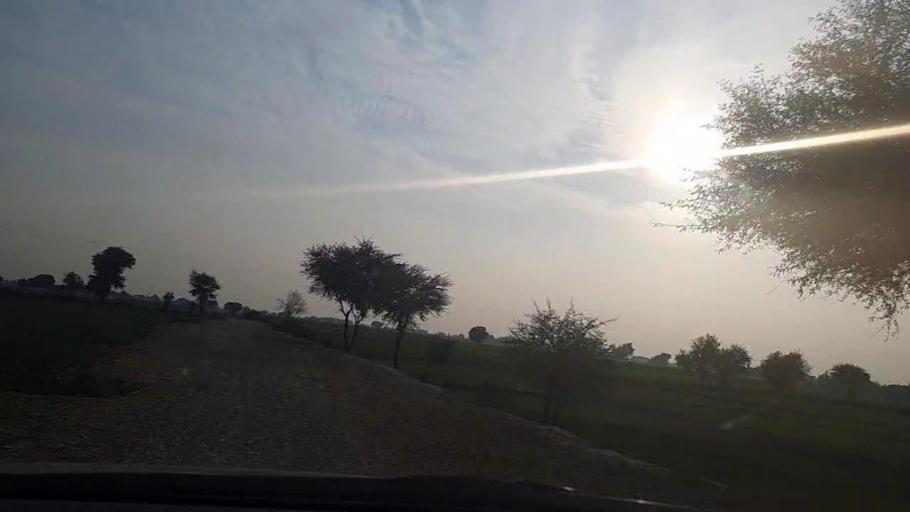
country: PK
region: Sindh
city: Daulatpur
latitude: 26.3333
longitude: 68.0229
